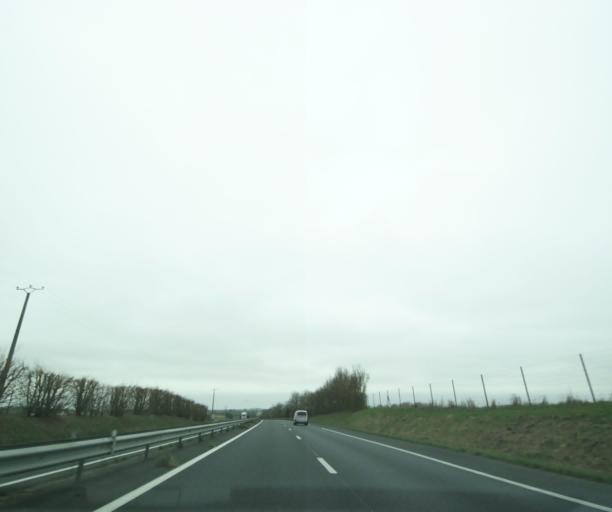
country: FR
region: Centre
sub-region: Departement de l'Indre
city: Vatan
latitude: 47.0719
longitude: 1.8225
